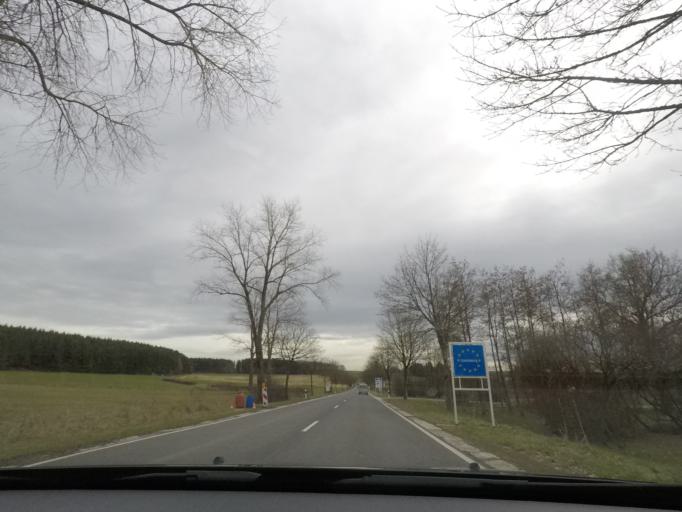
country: LU
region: Diekirch
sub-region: Canton de Wiltz
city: Winseler
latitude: 49.9813
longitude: 5.8381
